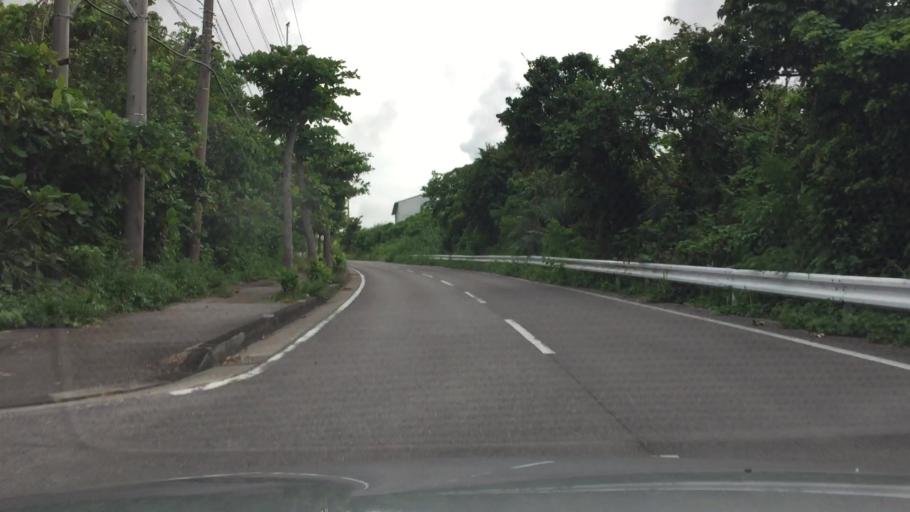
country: JP
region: Okinawa
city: Ishigaki
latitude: 24.4501
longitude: 124.1595
